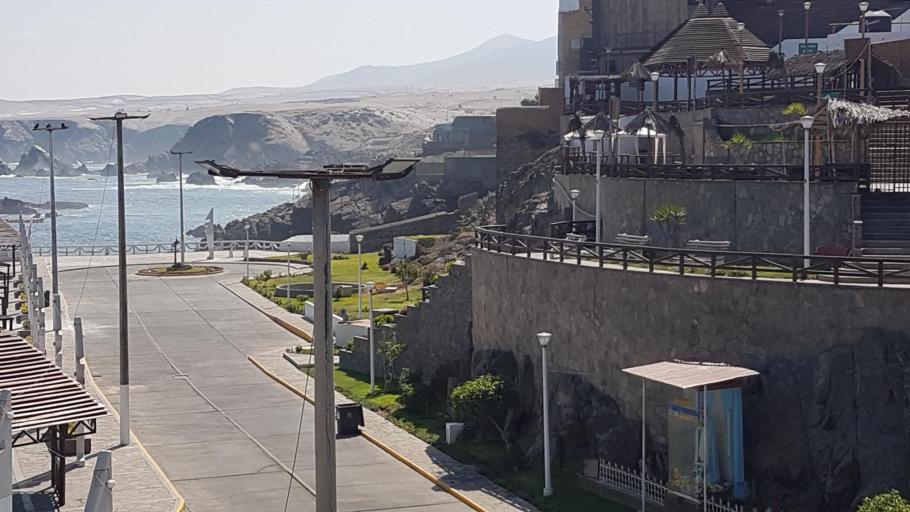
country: PE
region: Arequipa
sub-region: Provincia de Islay
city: Mollendo
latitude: -17.0317
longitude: -72.0153
